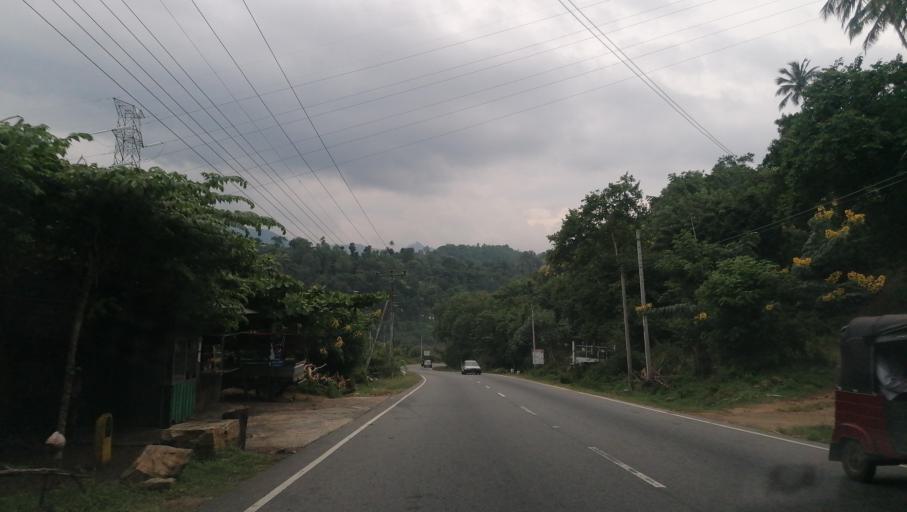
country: LK
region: Central
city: Kandy
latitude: 7.2462
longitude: 80.7302
